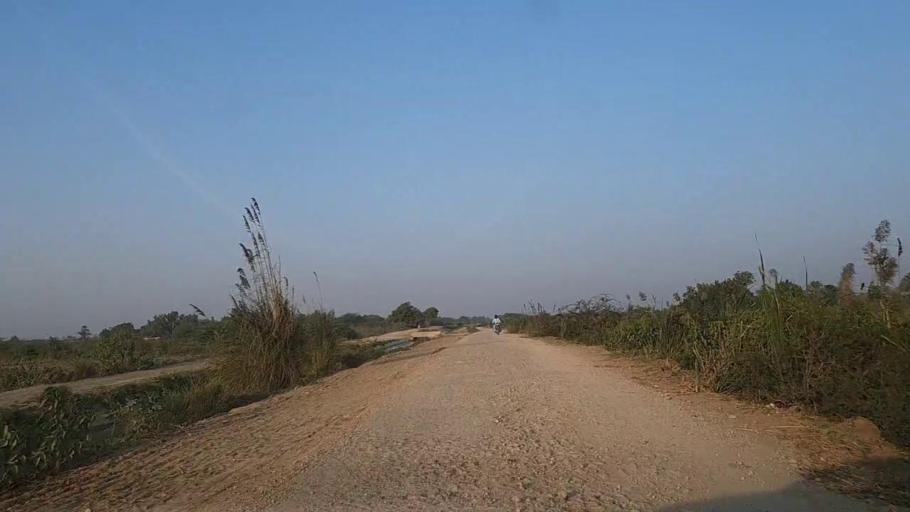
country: PK
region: Sindh
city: Mirpur Sakro
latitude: 24.2852
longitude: 67.6901
